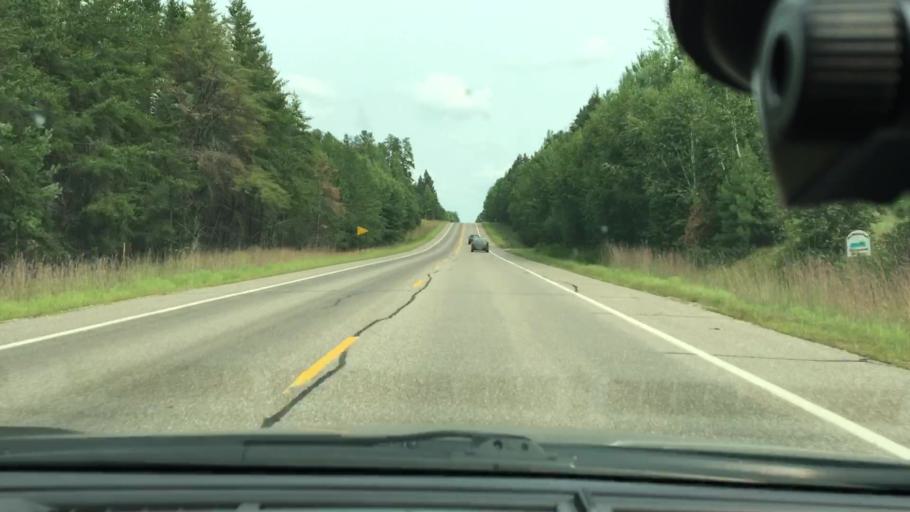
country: US
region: Minnesota
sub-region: Crow Wing County
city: Cross Lake
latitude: 46.7309
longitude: -93.9838
